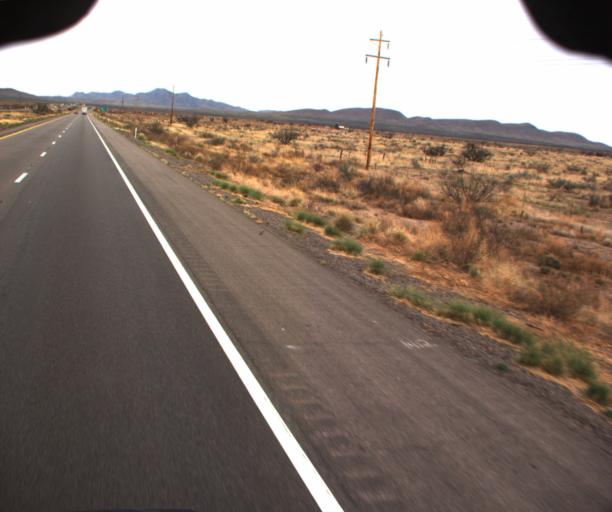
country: US
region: Arizona
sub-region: Cochise County
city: Willcox
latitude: 32.1828
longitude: -109.9391
